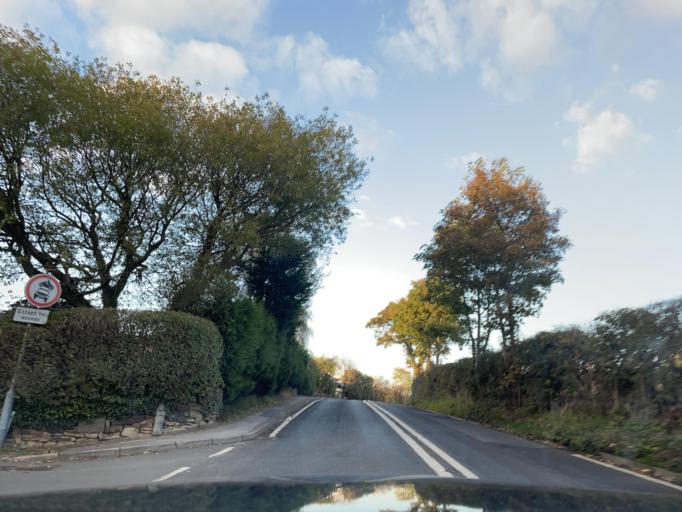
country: GB
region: England
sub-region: Borough of Stockport
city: Marple
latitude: 53.4086
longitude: -2.0405
